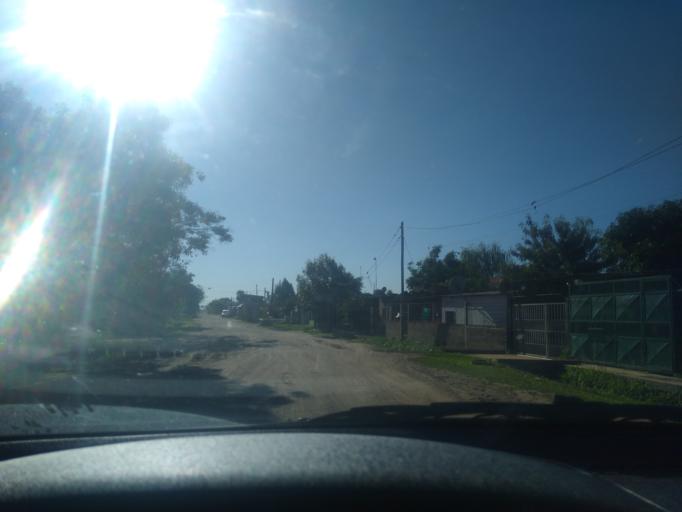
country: AR
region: Chaco
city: Puerto Vilelas
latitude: -27.5074
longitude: -58.9374
